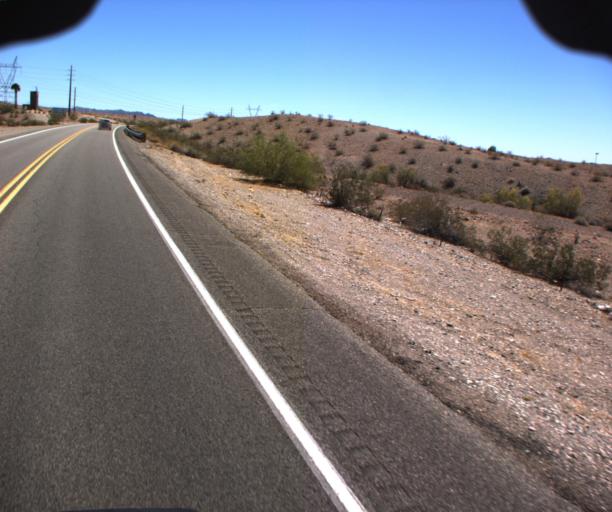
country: US
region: Arizona
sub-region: Mohave County
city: Lake Havasu City
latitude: 34.4506
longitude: -114.2471
